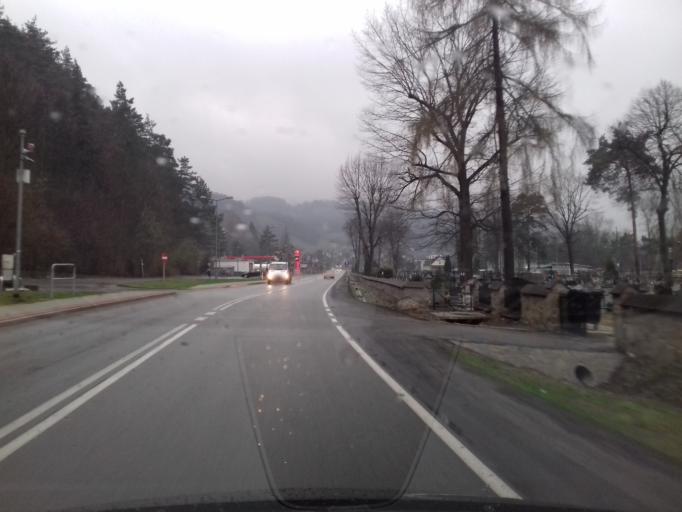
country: PL
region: Lesser Poland Voivodeship
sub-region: Powiat nowosadecki
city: Piwniczna-Zdroj
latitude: 49.4475
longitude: 20.7063
